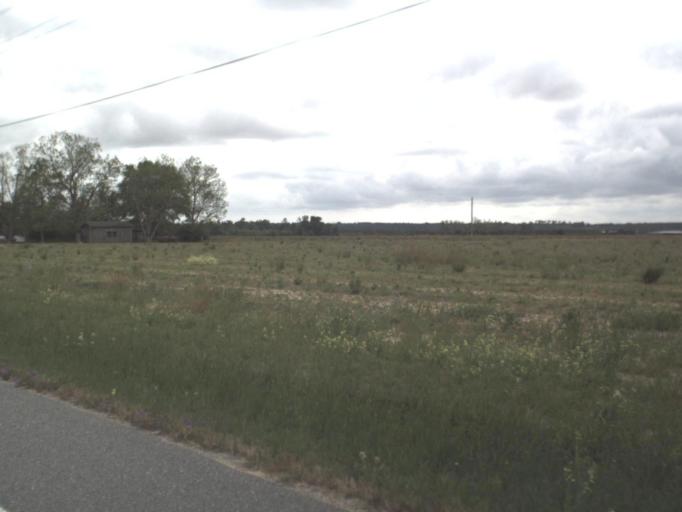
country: US
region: Florida
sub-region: Santa Rosa County
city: Point Baker
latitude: 30.8143
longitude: -87.0448
